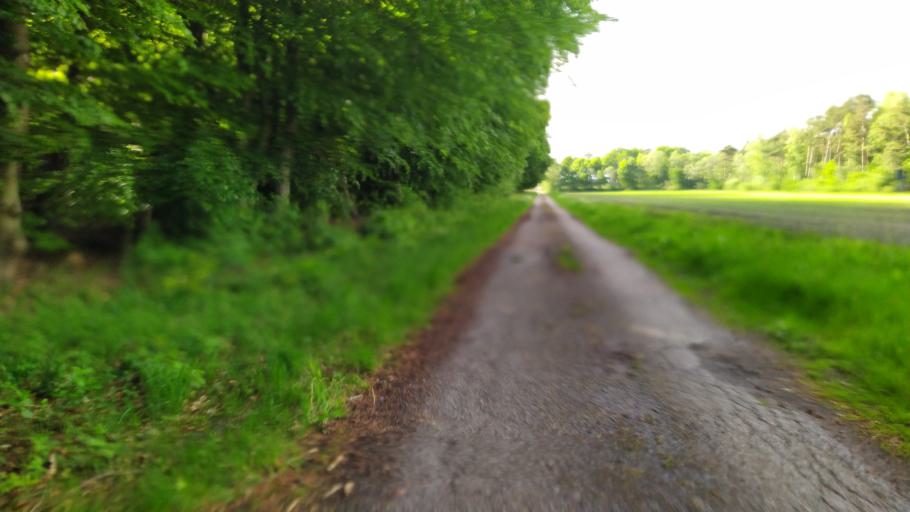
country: DE
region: Lower Saxony
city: Farven
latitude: 53.4429
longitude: 9.2849
